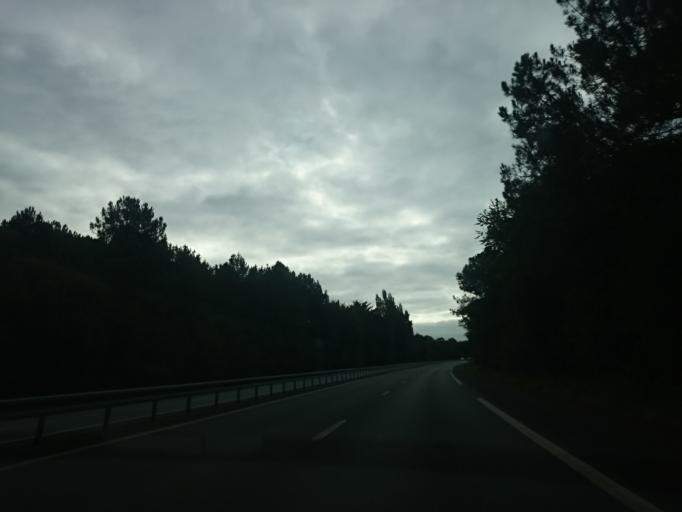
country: FR
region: Brittany
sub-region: Departement du Morbihan
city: Landevant
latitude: 47.7522
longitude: -3.1098
